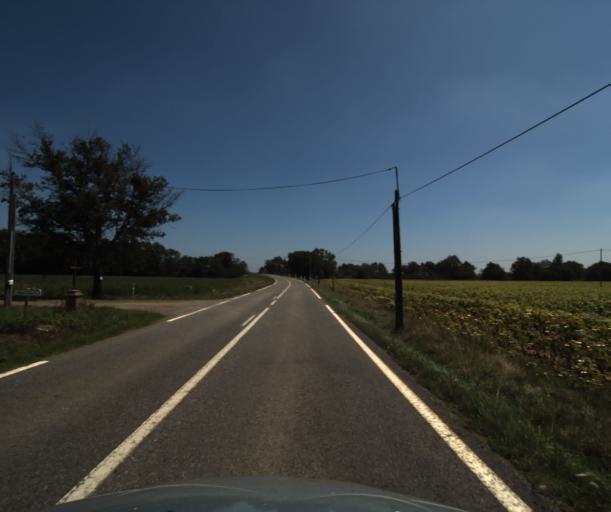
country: FR
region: Midi-Pyrenees
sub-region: Departement de la Haute-Garonne
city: Fonsorbes
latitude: 43.5054
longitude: 1.2412
